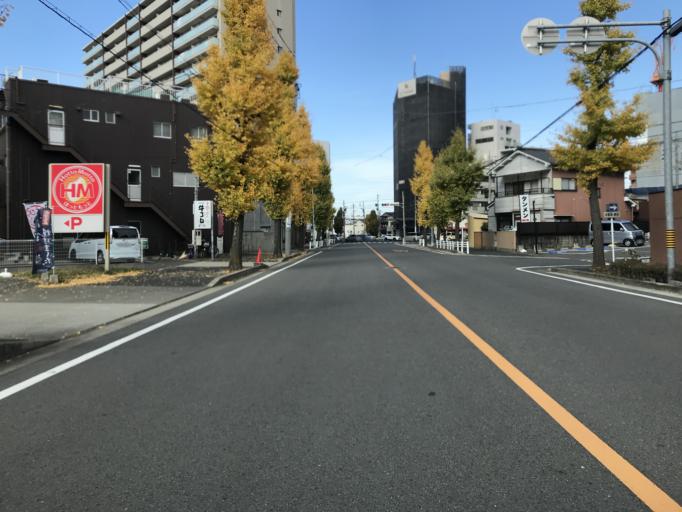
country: JP
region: Aichi
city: Nagoya-shi
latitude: 35.1955
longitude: 136.9222
